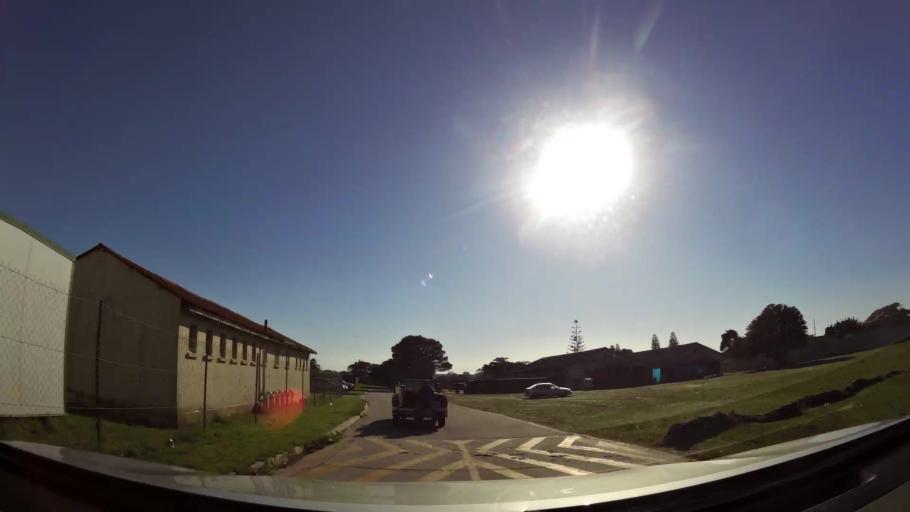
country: ZA
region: Eastern Cape
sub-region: Nelson Mandela Bay Metropolitan Municipality
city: Port Elizabeth
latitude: -33.9858
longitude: 25.6284
